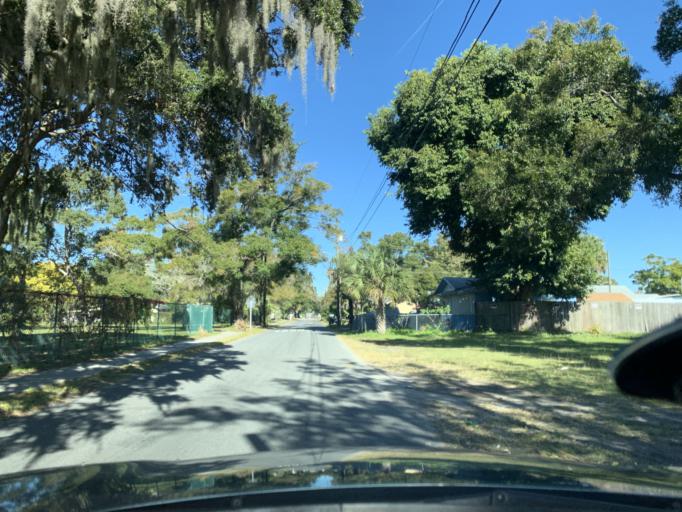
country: US
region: Florida
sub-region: Pinellas County
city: Gulfport
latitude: 27.7504
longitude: -82.7017
